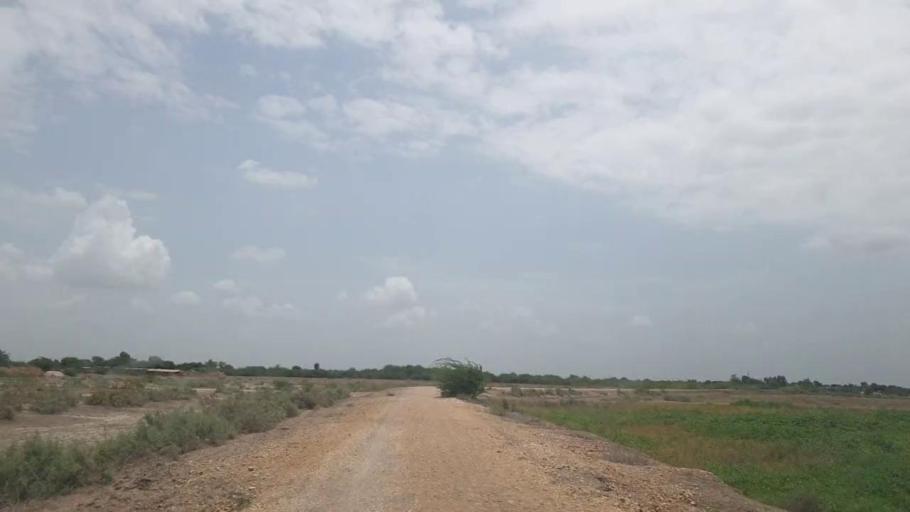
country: PK
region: Sindh
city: Naukot
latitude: 24.9120
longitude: 69.2032
